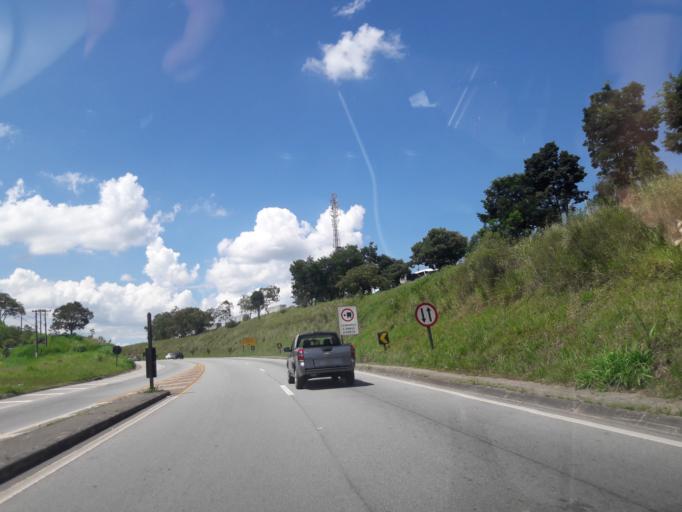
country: BR
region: Sao Paulo
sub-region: Cajamar
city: Cajamar
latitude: -23.3398
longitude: -46.8259
